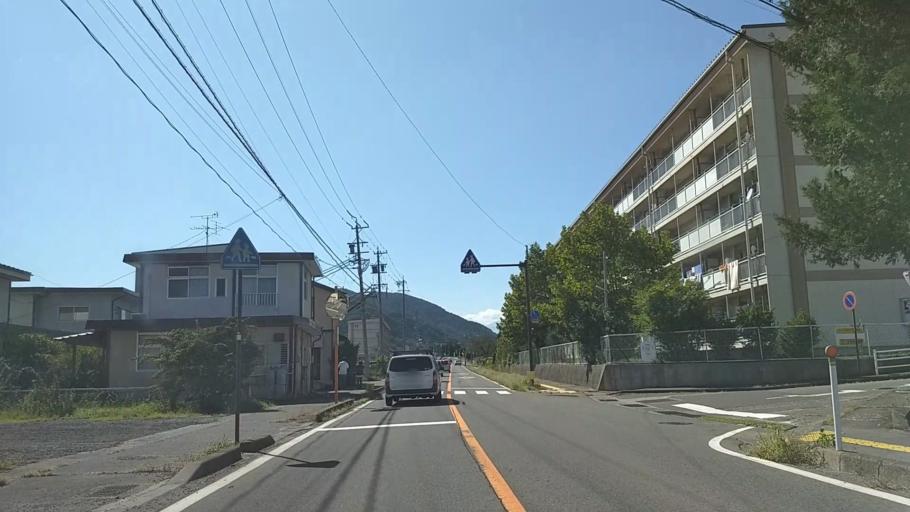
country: JP
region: Nagano
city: Nagano-shi
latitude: 36.6227
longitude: 138.1452
